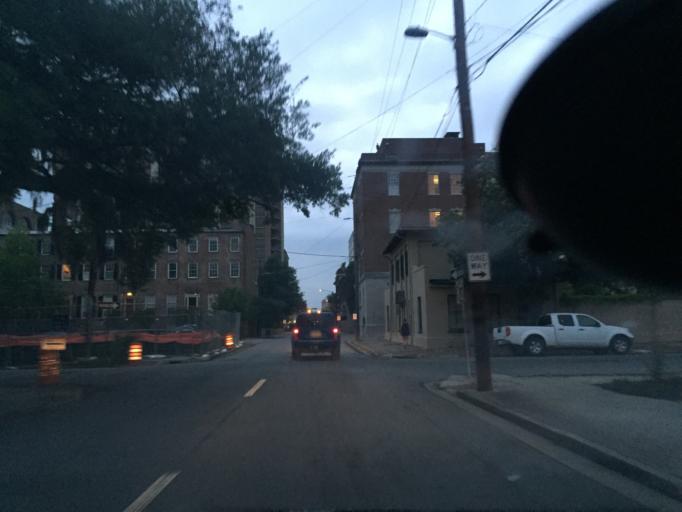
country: US
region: Georgia
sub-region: Chatham County
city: Savannah
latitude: 32.0727
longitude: -81.0930
